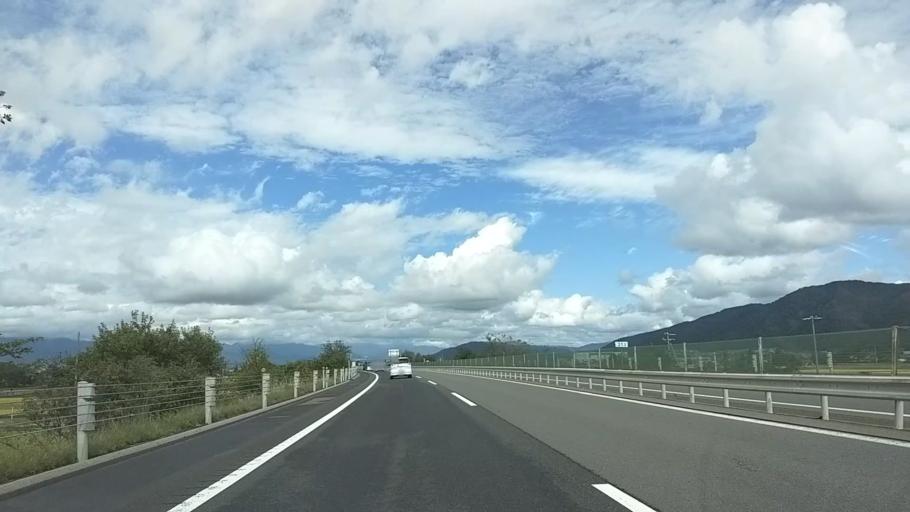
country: JP
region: Nagano
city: Toyoshina
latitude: 36.2826
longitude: 137.9307
